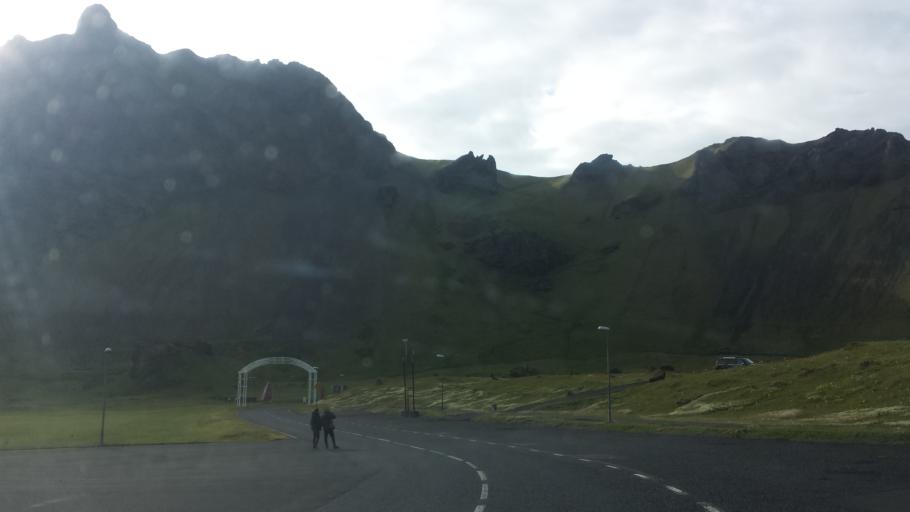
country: IS
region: South
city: Vestmannaeyjar
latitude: 63.4409
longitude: -20.2946
